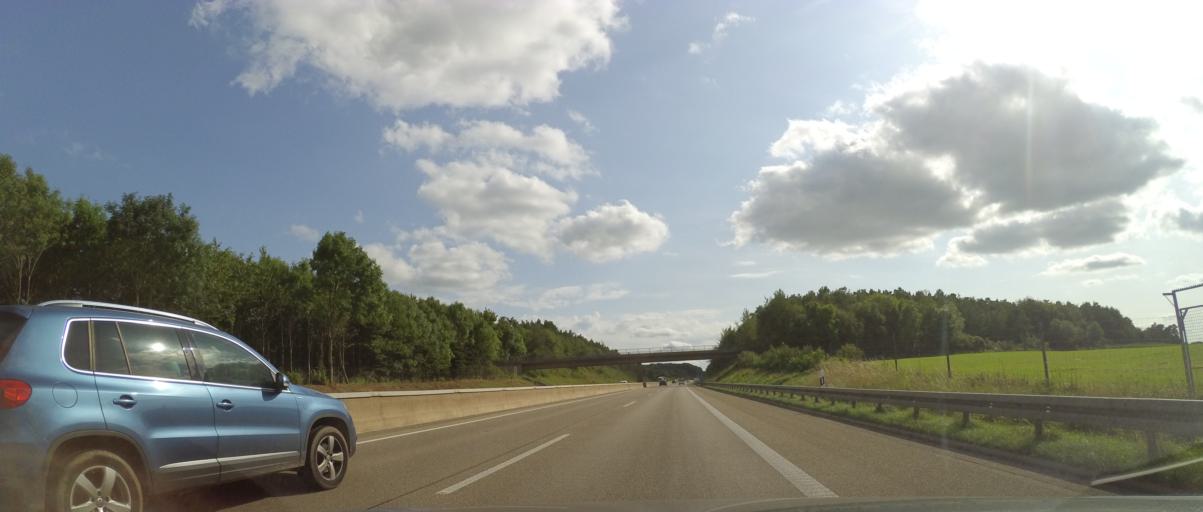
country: DE
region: North Rhine-Westphalia
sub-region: Regierungsbezirk Koln
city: Mechernich
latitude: 50.5432
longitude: 6.6774
